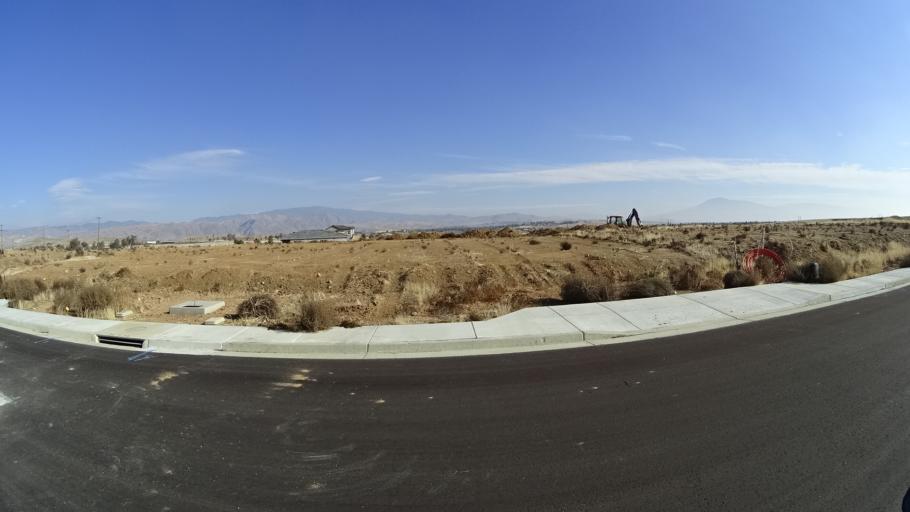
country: US
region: California
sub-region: Kern County
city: Oildale
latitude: 35.4098
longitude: -118.9041
